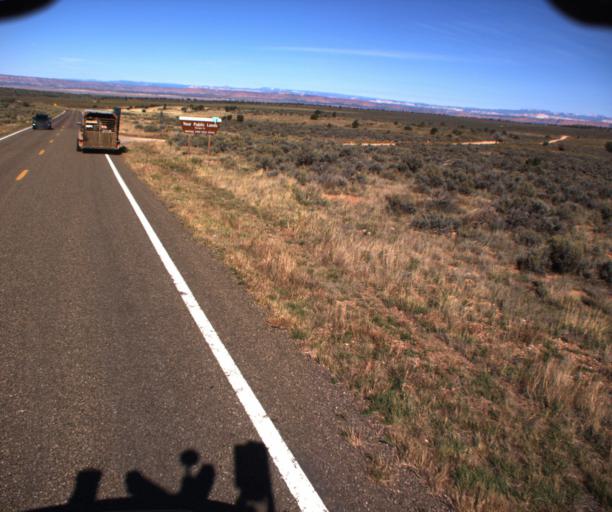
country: US
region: Arizona
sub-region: Coconino County
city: Fredonia
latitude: 36.8487
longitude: -112.2860
